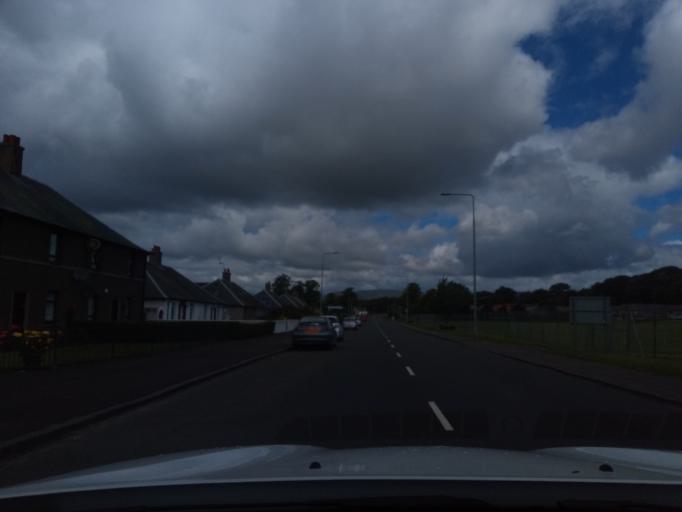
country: GB
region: Scotland
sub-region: Fife
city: Kincardine
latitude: 56.0707
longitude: -3.7191
